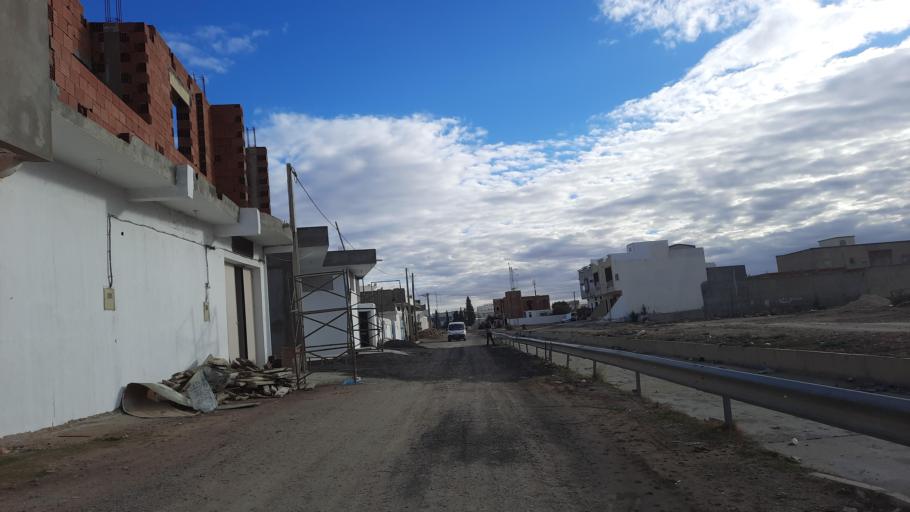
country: TN
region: Al Mahdiyah
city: El Jem
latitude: 35.2883
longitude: 10.7037
